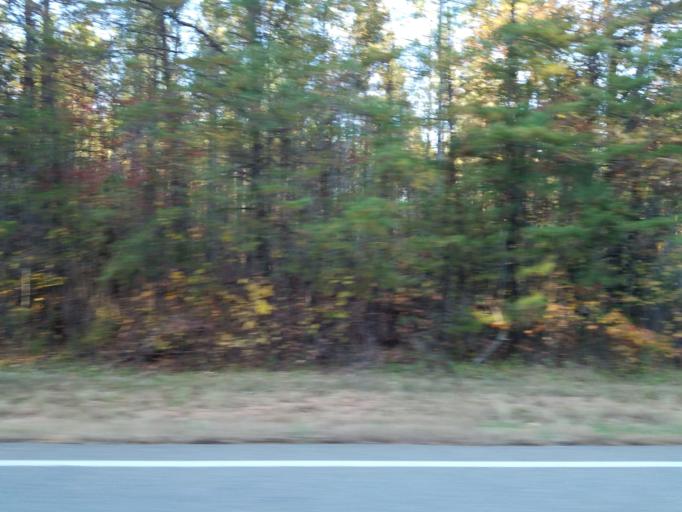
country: US
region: Georgia
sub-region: Dawson County
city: Dawsonville
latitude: 34.5400
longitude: -84.2161
